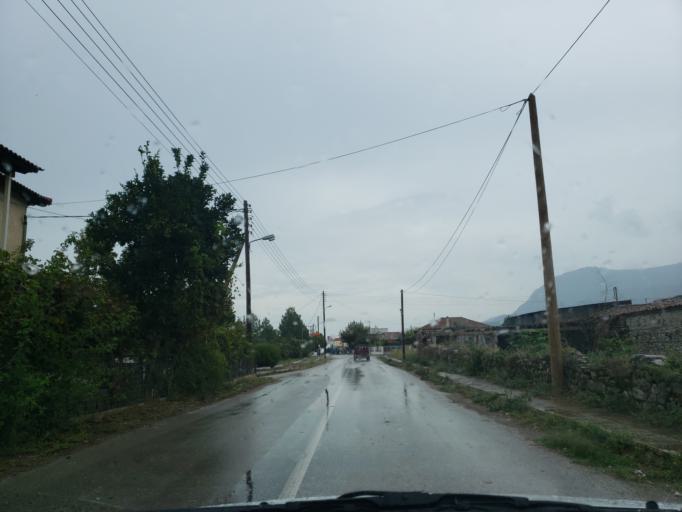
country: GR
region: Central Greece
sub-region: Nomos Fthiotidos
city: Anthili
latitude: 38.8045
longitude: 22.4442
